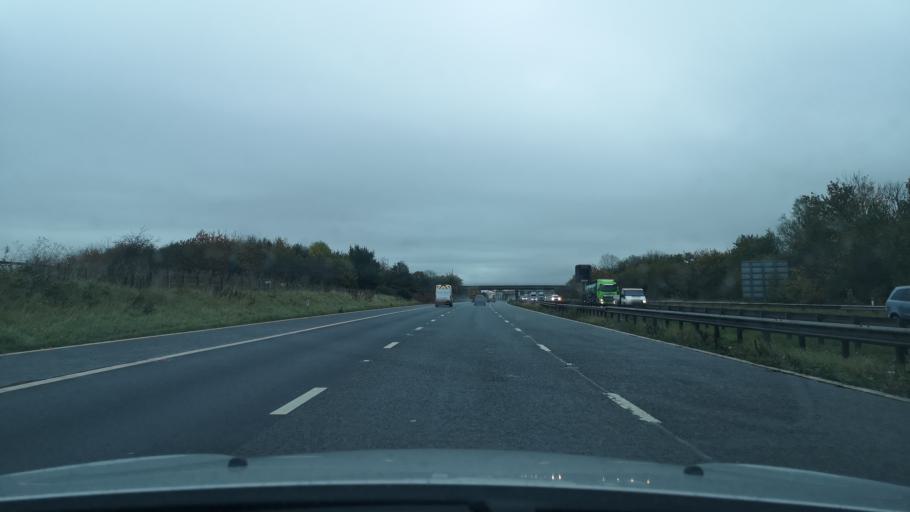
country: GB
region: England
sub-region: East Riding of Yorkshire
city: Pollington
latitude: 53.6943
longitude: -1.1244
